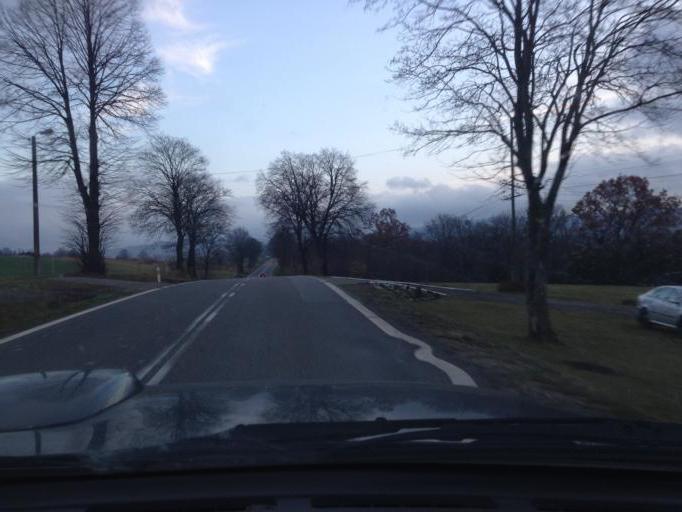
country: PL
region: Subcarpathian Voivodeship
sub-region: Powiat jasielski
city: Nowy Zmigrod
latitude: 49.6299
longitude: 21.5307
